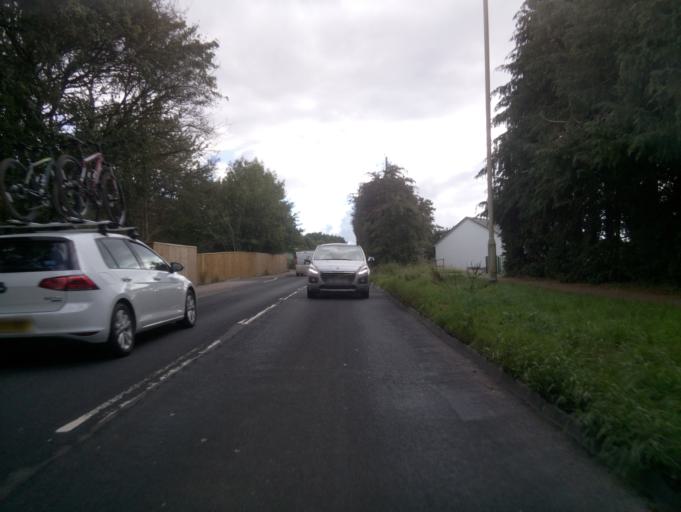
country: GB
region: England
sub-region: Devon
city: Honiton
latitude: 50.7931
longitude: -3.2022
